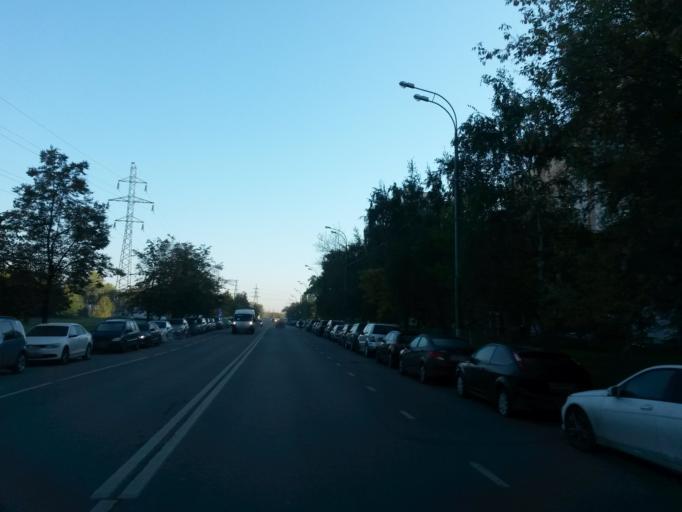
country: RU
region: Moscow
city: Mar'ino
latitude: 55.6531
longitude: 37.7104
